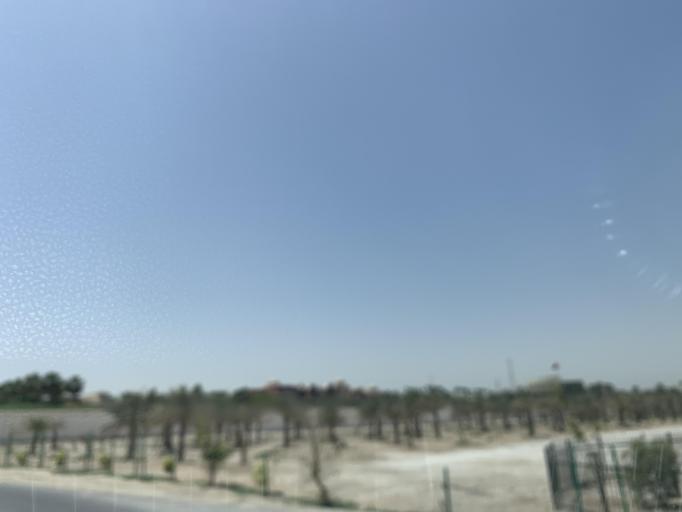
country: BH
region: Northern
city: Ar Rifa'
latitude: 26.1485
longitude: 50.5545
